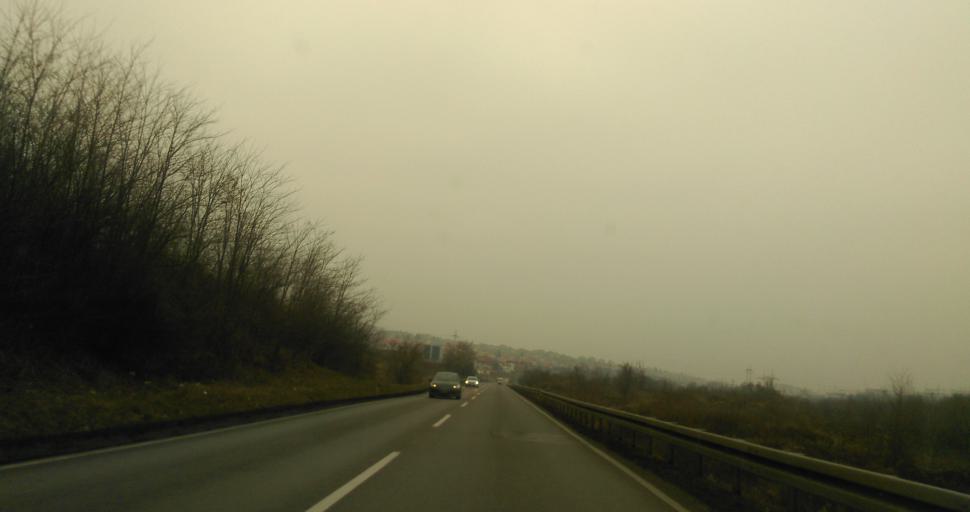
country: RS
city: Rusanj
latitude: 44.7156
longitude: 20.4750
